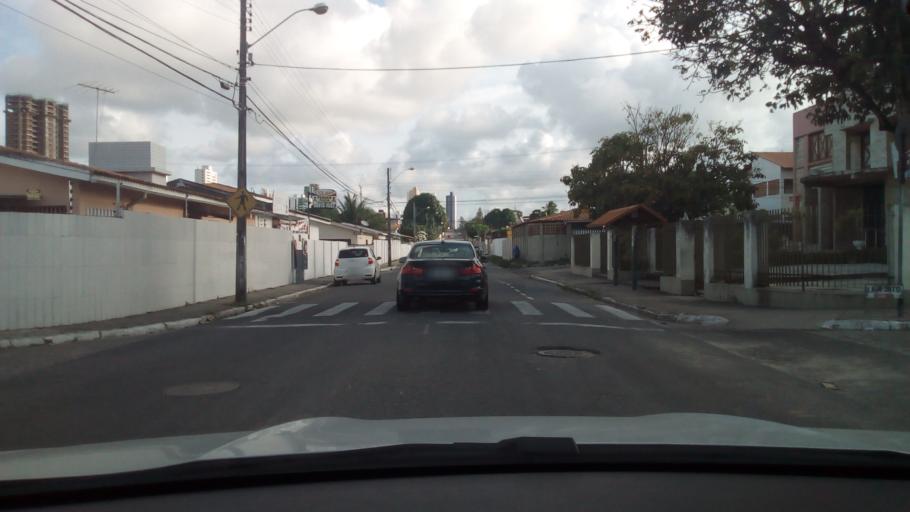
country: BR
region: Paraiba
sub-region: Joao Pessoa
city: Joao Pessoa
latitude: -7.1019
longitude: -34.8578
